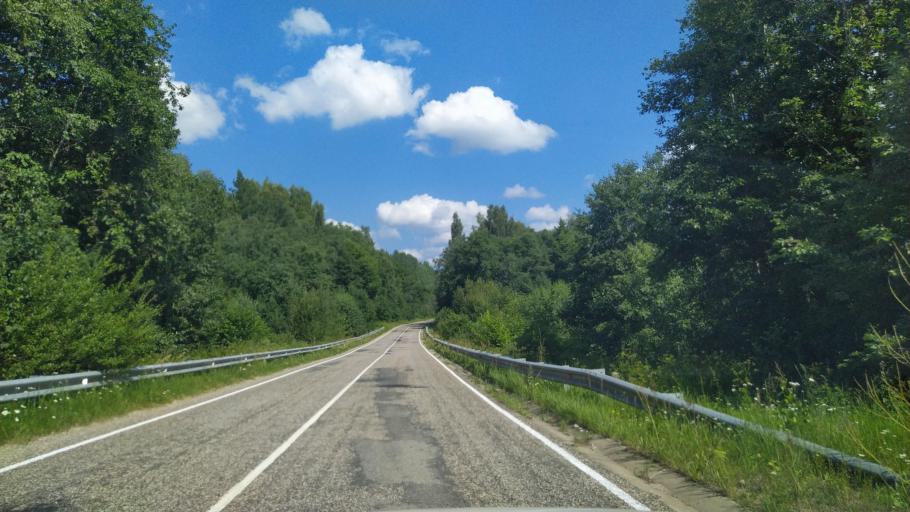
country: RU
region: Pskov
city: Pushkinskiye Gory
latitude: 57.0629
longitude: 28.9491
